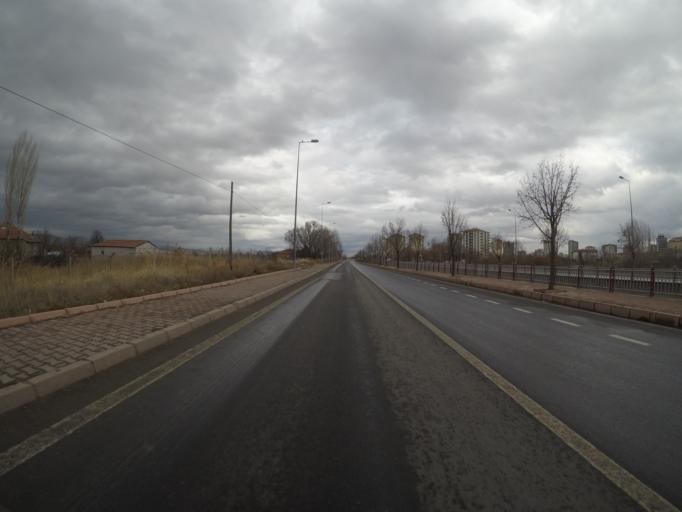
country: TR
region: Kayseri
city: Kayseri
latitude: 38.7558
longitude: 35.4786
